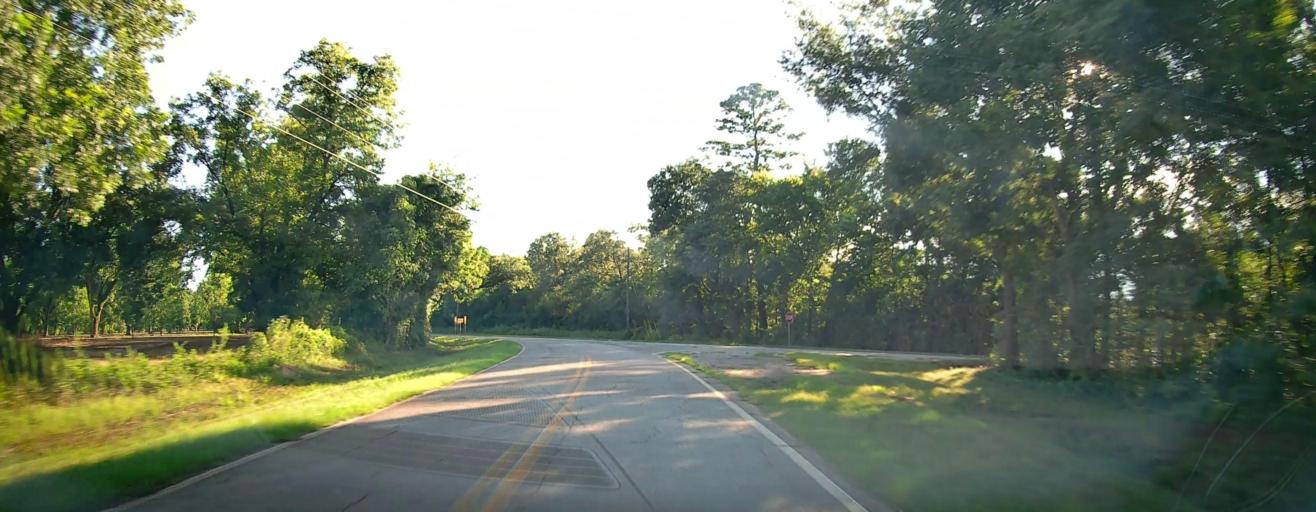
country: US
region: Georgia
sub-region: Bleckley County
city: Cochran
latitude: 32.3903
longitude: -83.4538
